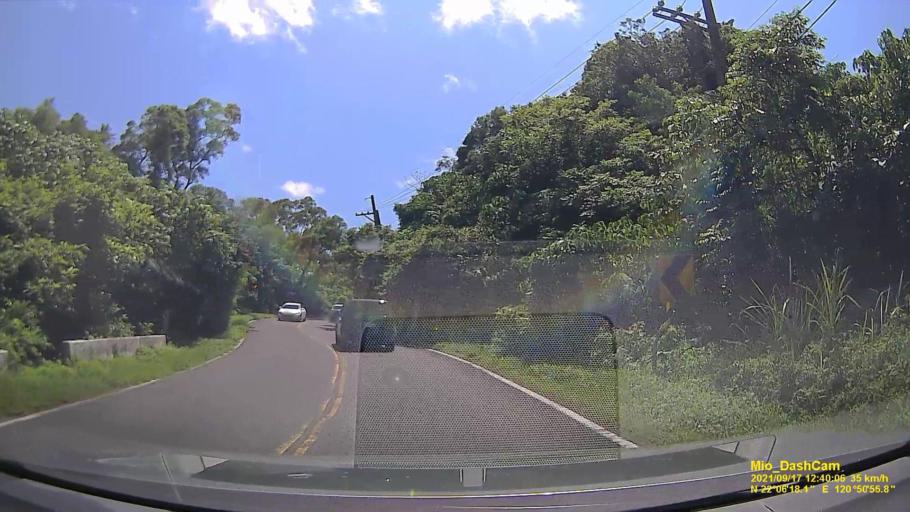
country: TW
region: Taiwan
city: Hengchun
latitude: 22.1050
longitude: 120.8488
